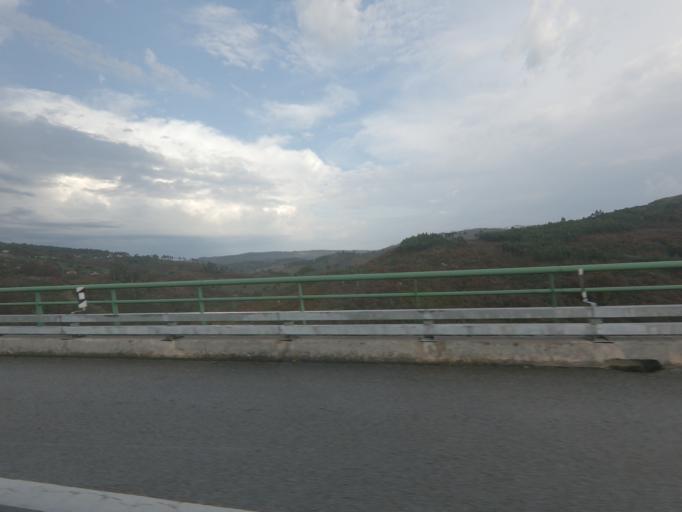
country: PT
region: Viseu
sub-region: Castro Daire
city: Castro Daire
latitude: 40.8891
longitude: -7.9196
